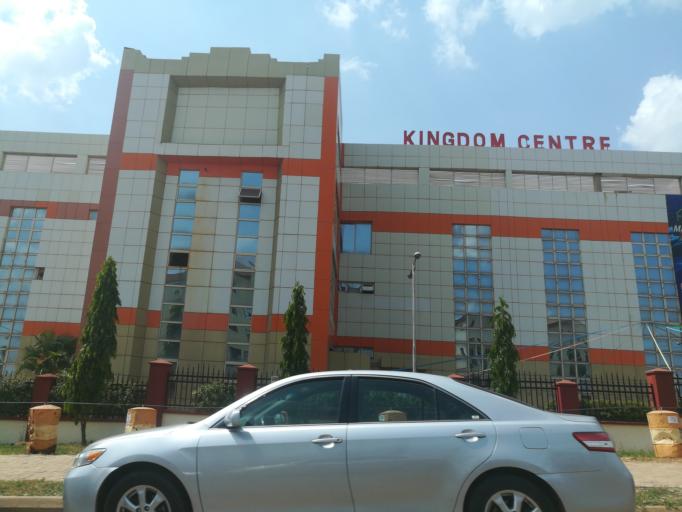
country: NG
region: Abuja Federal Capital Territory
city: Abuja
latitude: 9.0593
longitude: 7.4447
